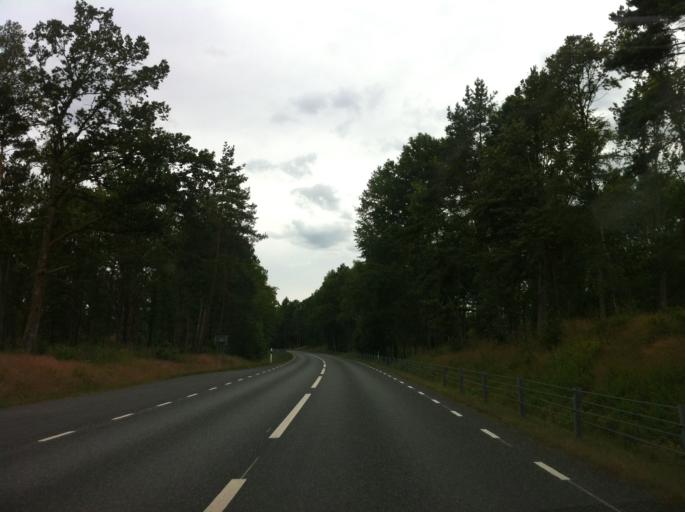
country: SE
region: Skane
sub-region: Hassleholms Kommun
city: Hastveda
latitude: 56.2332
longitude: 13.9983
